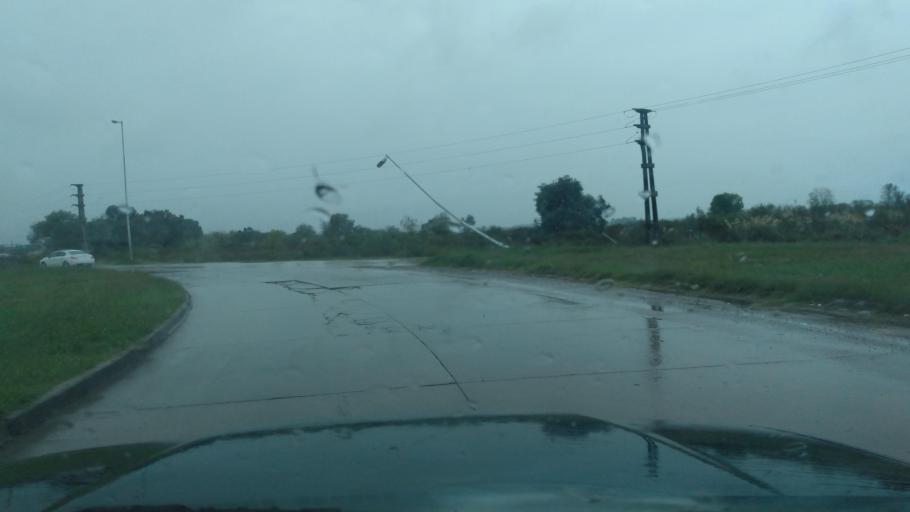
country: AR
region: Buenos Aires
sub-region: Partido de Campana
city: Campana
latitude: -34.2026
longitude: -58.9605
